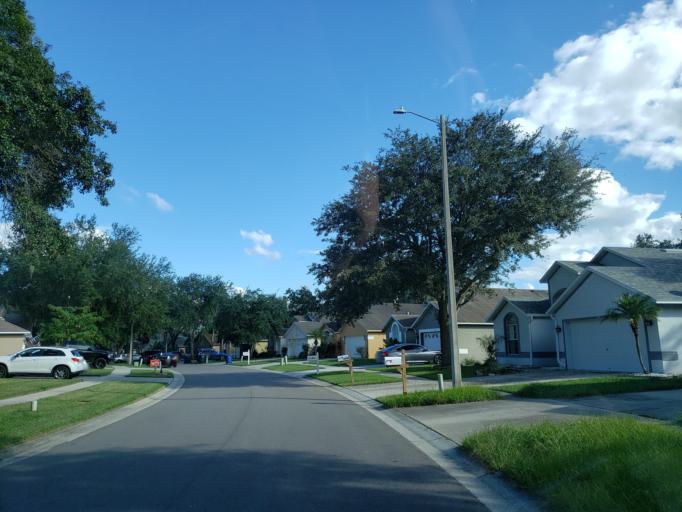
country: US
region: Florida
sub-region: Hillsborough County
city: Bloomingdale
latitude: 27.8838
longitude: -82.2438
